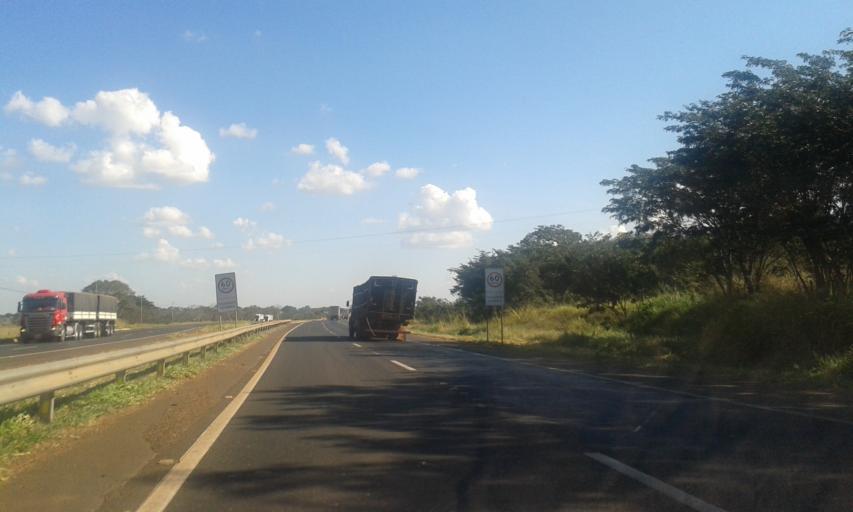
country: BR
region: Minas Gerais
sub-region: Monte Alegre De Minas
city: Monte Alegre de Minas
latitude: -18.8691
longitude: -48.5963
